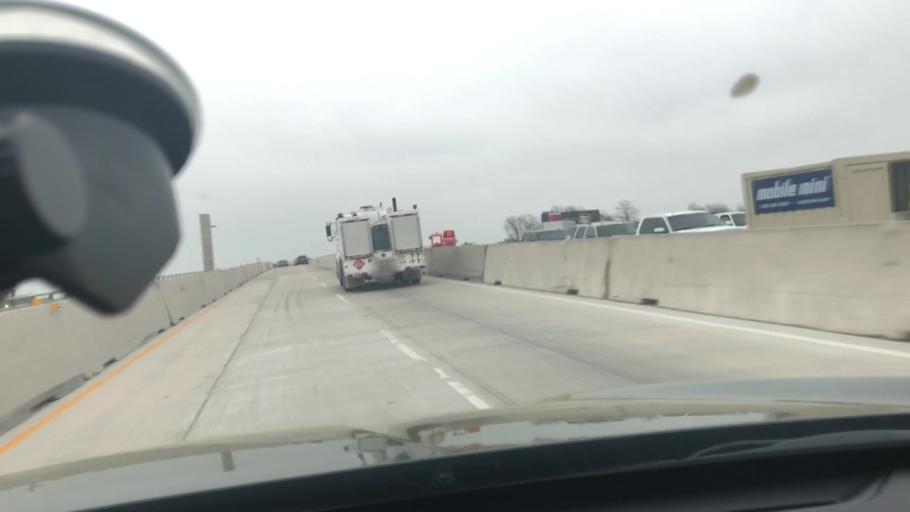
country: US
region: Texas
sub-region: Bell County
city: Temple
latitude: 31.0958
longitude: -97.3702
